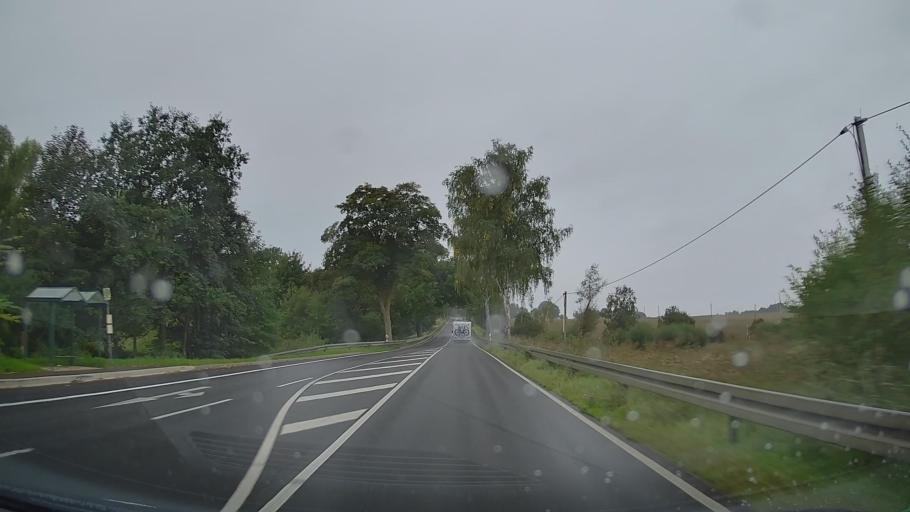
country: DE
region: Mecklenburg-Vorpommern
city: Gaegelow
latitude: 53.7140
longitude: 11.8824
